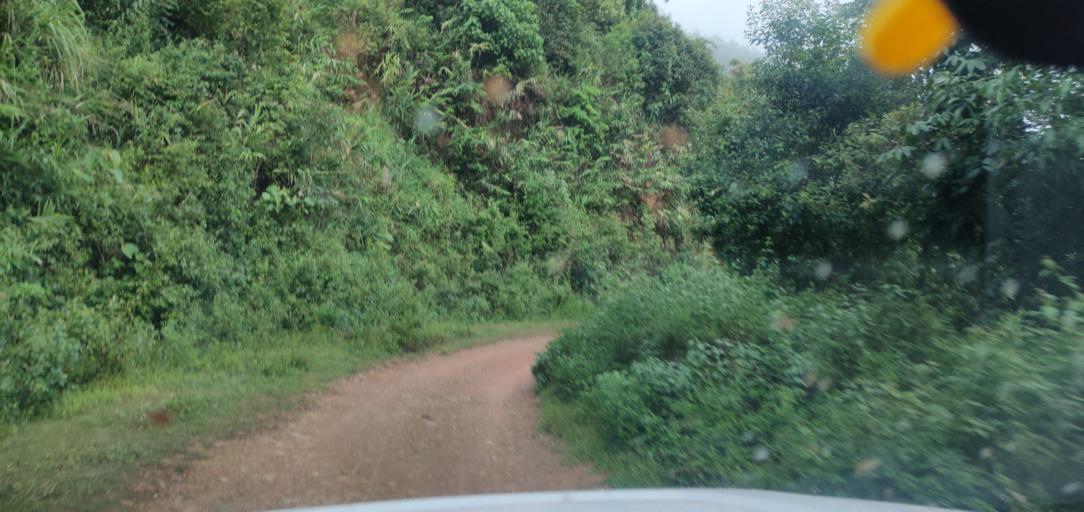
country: LA
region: Phongsali
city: Phongsali
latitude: 21.4486
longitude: 102.2843
